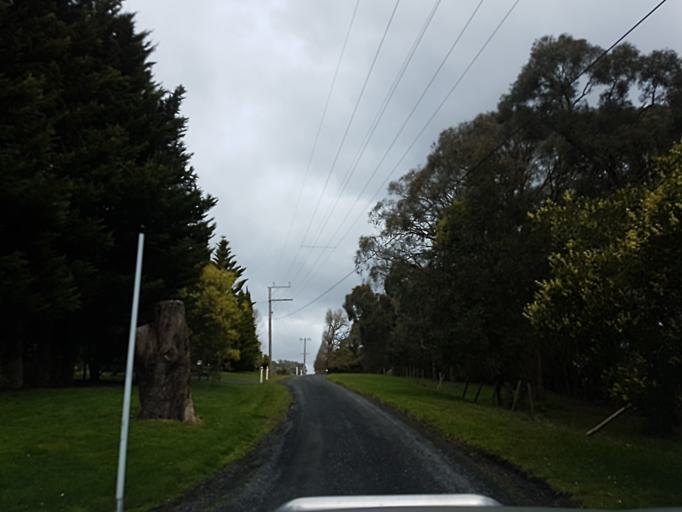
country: AU
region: Victoria
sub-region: Cardinia
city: Emerald
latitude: -37.8961
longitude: 145.4353
